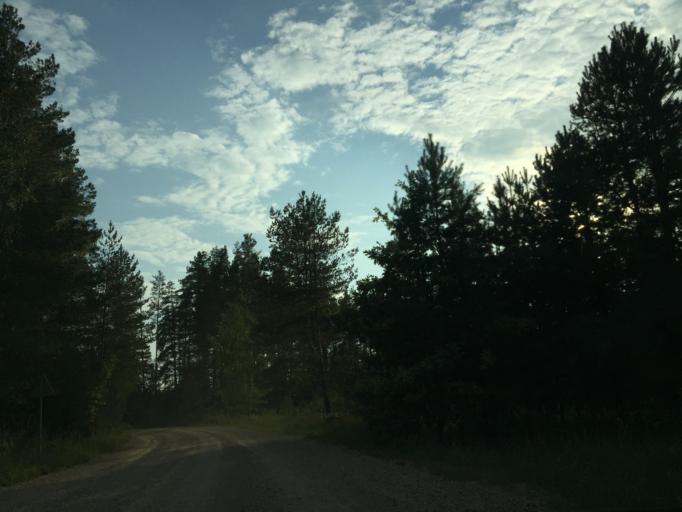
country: LV
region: Ikskile
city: Ikskile
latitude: 56.8070
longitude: 24.4421
